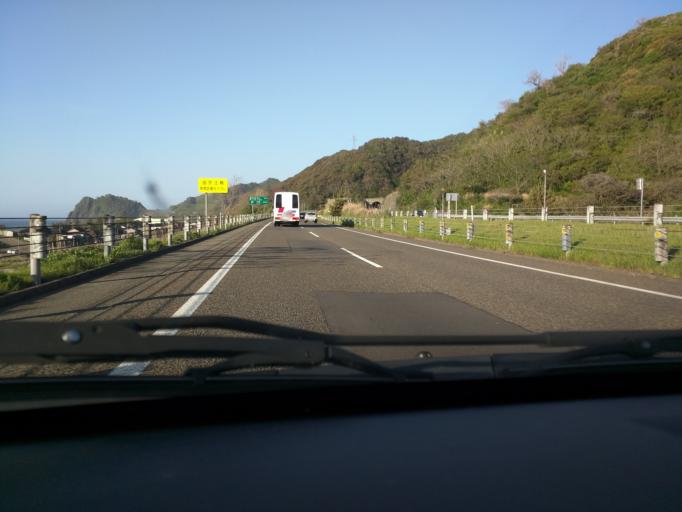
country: JP
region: Niigata
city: Kashiwazaki
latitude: 37.3111
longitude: 138.4265
